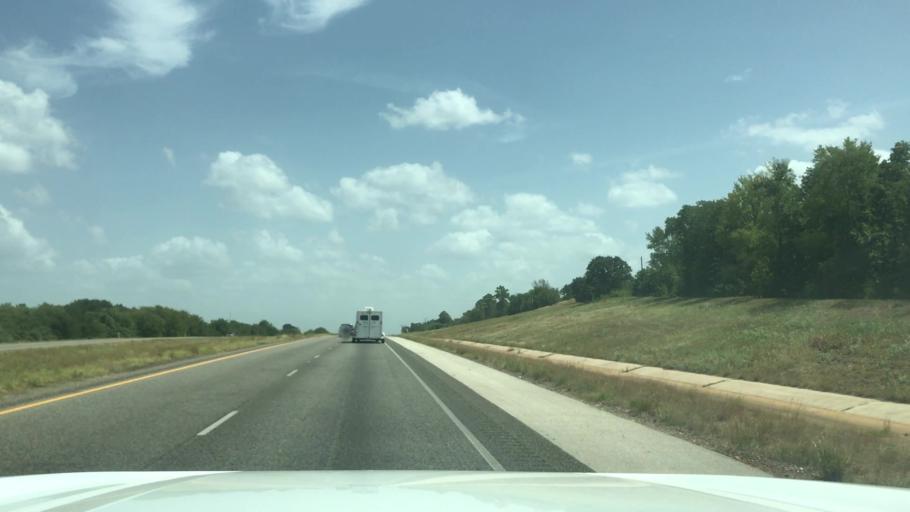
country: US
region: Texas
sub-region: Robertson County
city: Calvert
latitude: 30.9311
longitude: -96.6340
